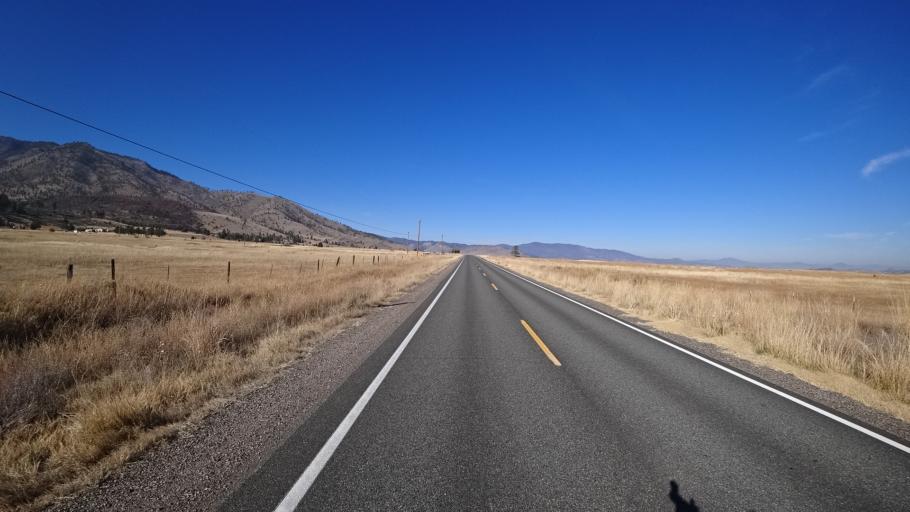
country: US
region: California
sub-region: Siskiyou County
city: Weed
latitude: 41.4728
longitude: -122.4818
